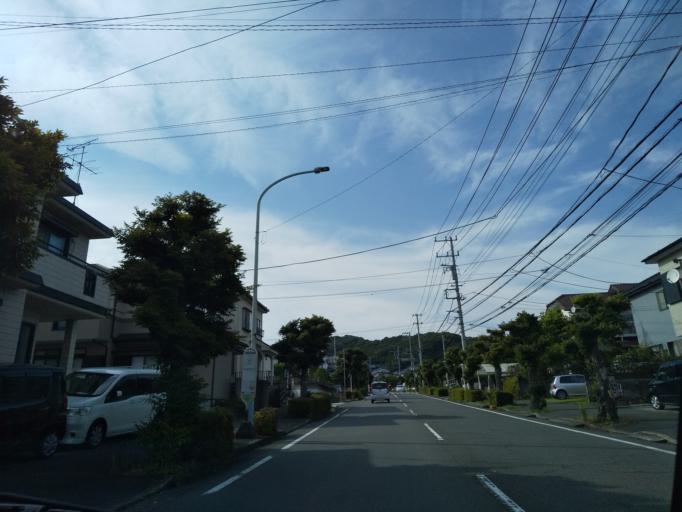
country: JP
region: Kanagawa
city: Zama
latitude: 35.4897
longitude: 139.3354
